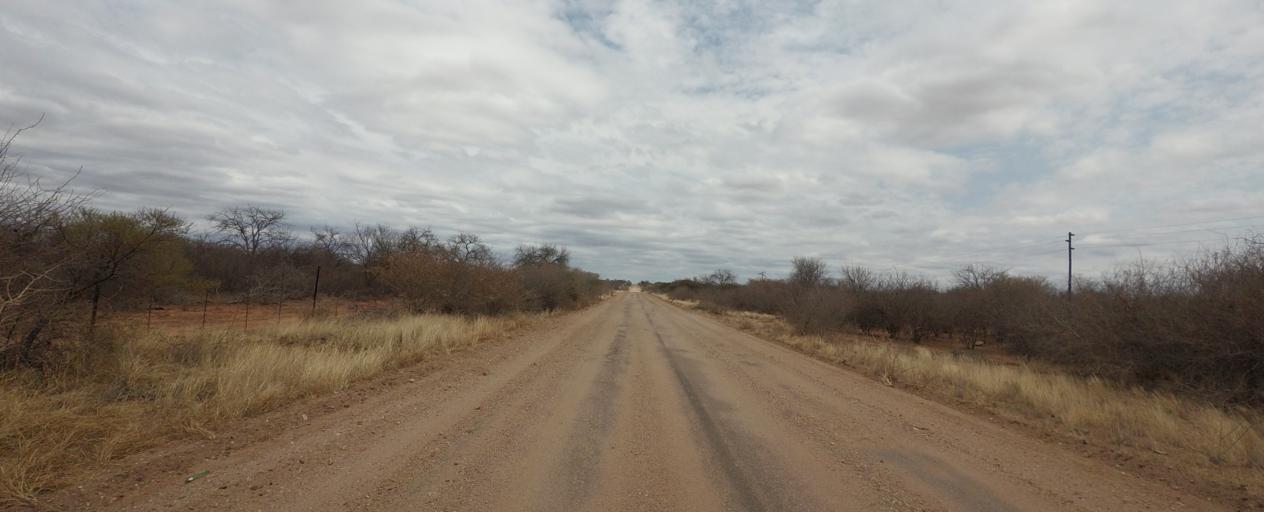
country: BW
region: Central
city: Mathathane
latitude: -22.6740
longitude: 28.6757
